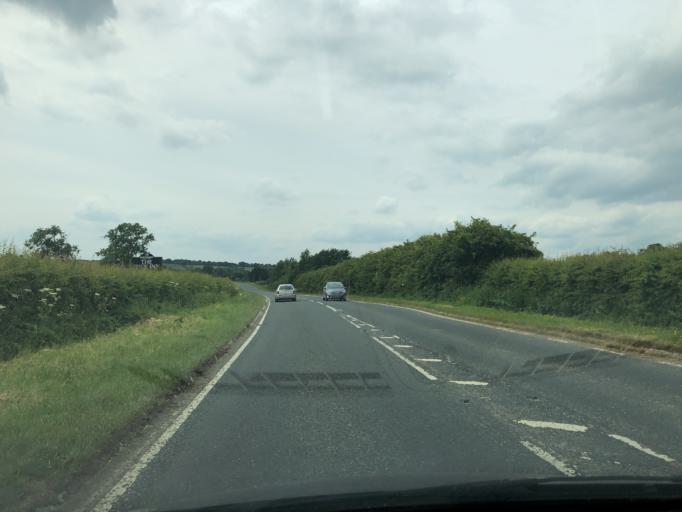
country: GB
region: England
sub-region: North Yorkshire
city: Pickering
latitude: 54.2625
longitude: -0.8173
